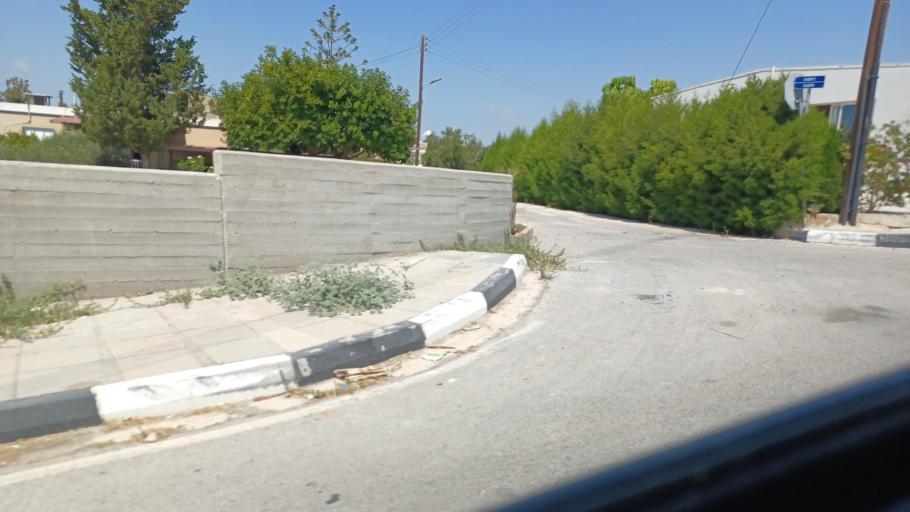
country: CY
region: Pafos
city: Mesogi
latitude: 34.7870
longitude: 32.4606
